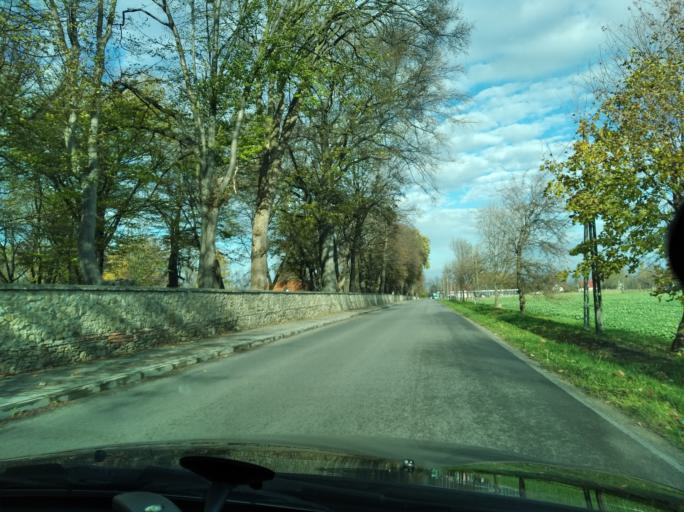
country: PL
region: Subcarpathian Voivodeship
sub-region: Powiat debicki
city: Brzeznica
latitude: 50.0567
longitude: 21.4840
